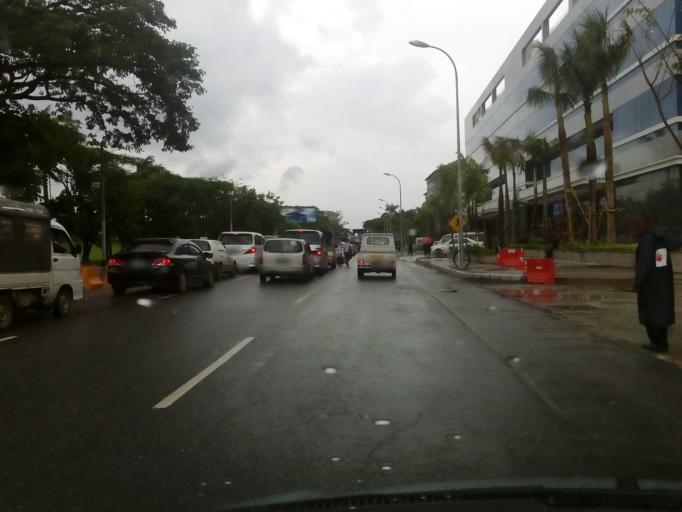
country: MM
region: Yangon
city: Yangon
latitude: 16.8272
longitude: 96.1544
